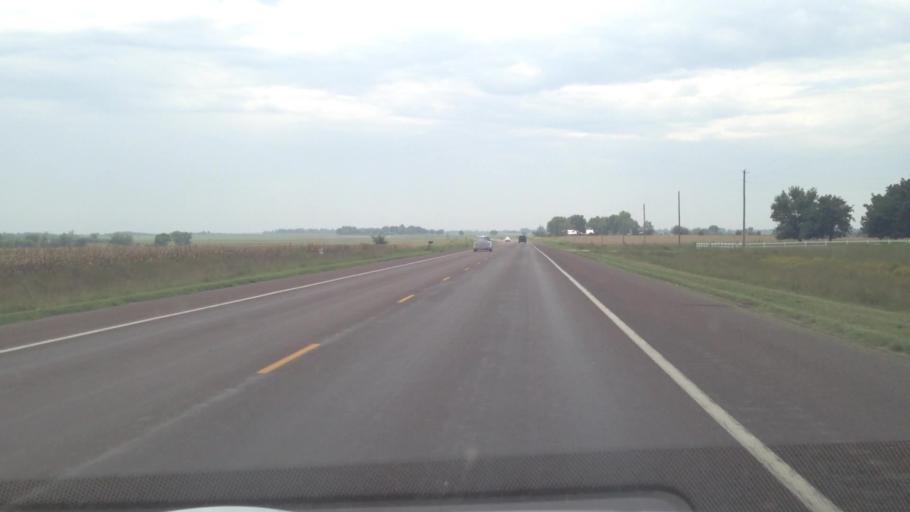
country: US
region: Kansas
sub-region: Crawford County
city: Girard
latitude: 37.4912
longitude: -94.8425
